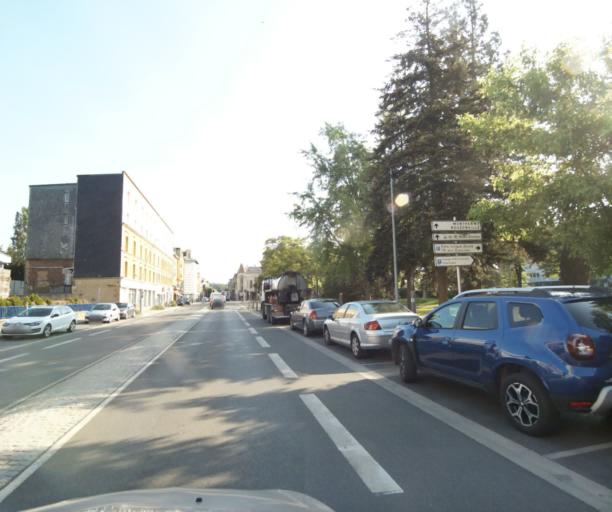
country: FR
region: Champagne-Ardenne
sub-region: Departement des Ardennes
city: Charleville-Mezieres
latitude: 49.7684
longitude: 4.7235
